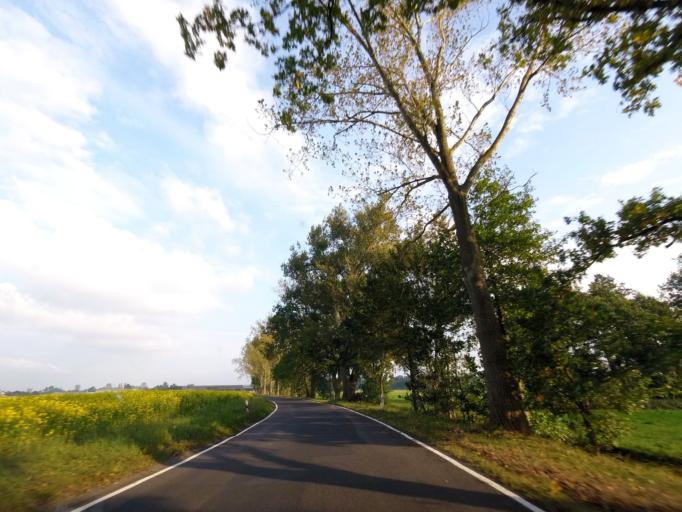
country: DE
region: Brandenburg
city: Linthe
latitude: 52.1502
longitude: 12.8304
